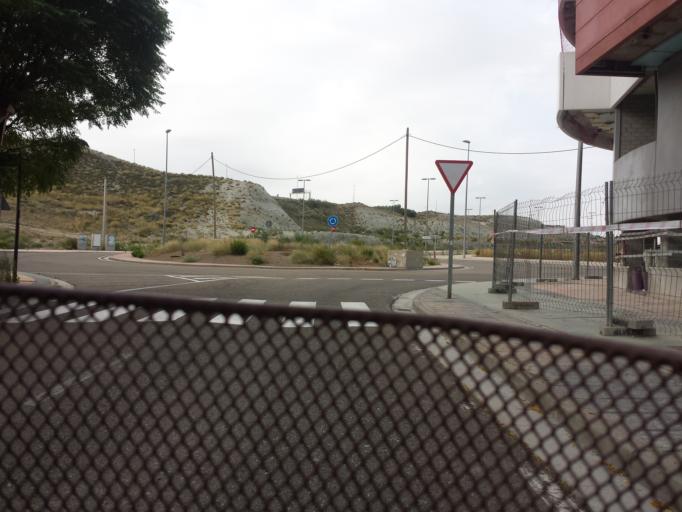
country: ES
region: Aragon
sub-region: Provincia de Zaragoza
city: Montecanal
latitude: 41.6214
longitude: -0.9465
